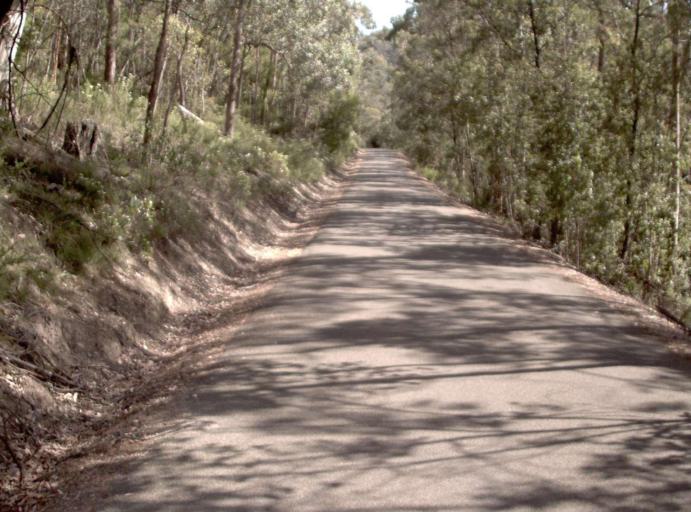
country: AU
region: Victoria
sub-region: East Gippsland
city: Lakes Entrance
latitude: -37.4698
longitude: 148.1240
